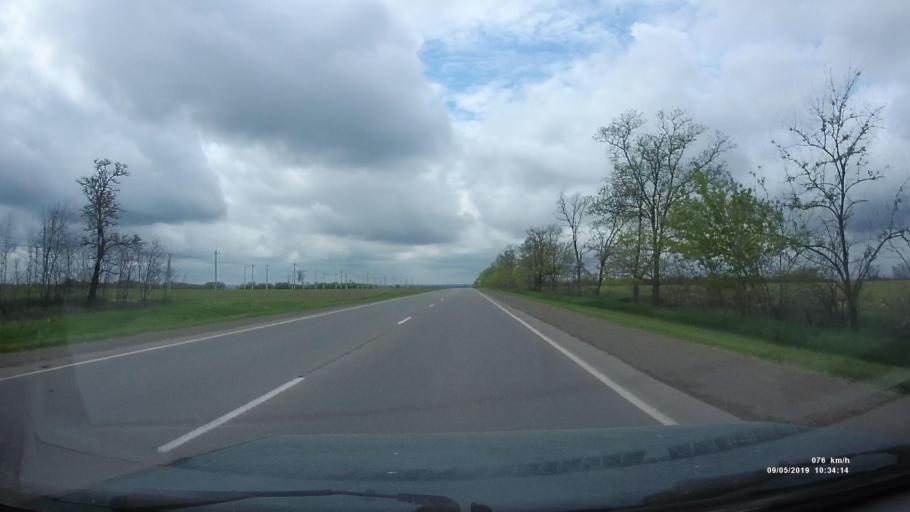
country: RU
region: Rostov
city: Peshkovo
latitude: 47.0565
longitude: 39.4211
